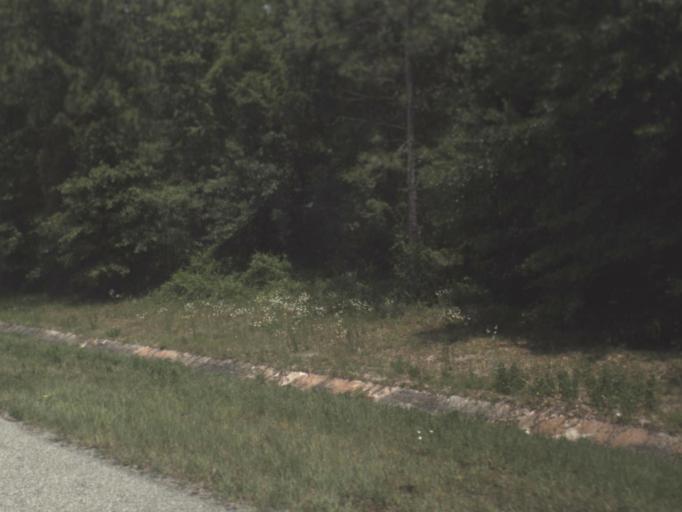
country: US
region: Florida
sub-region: Baker County
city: Macclenny
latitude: 30.1235
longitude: -82.0434
